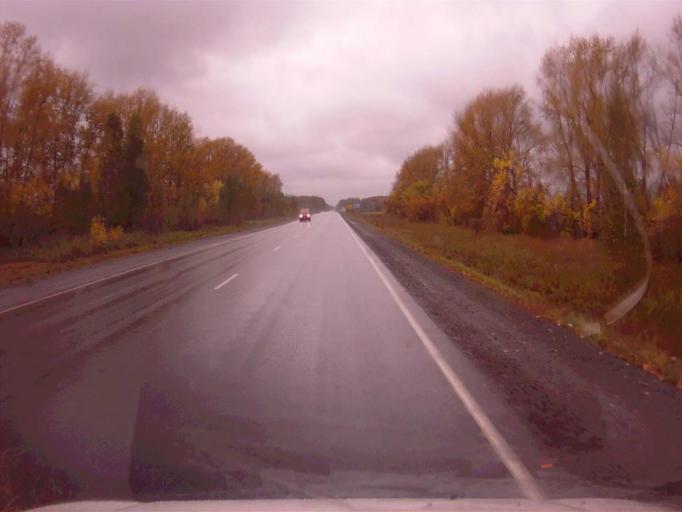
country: RU
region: Chelyabinsk
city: Argayash
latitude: 55.4529
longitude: 60.9332
